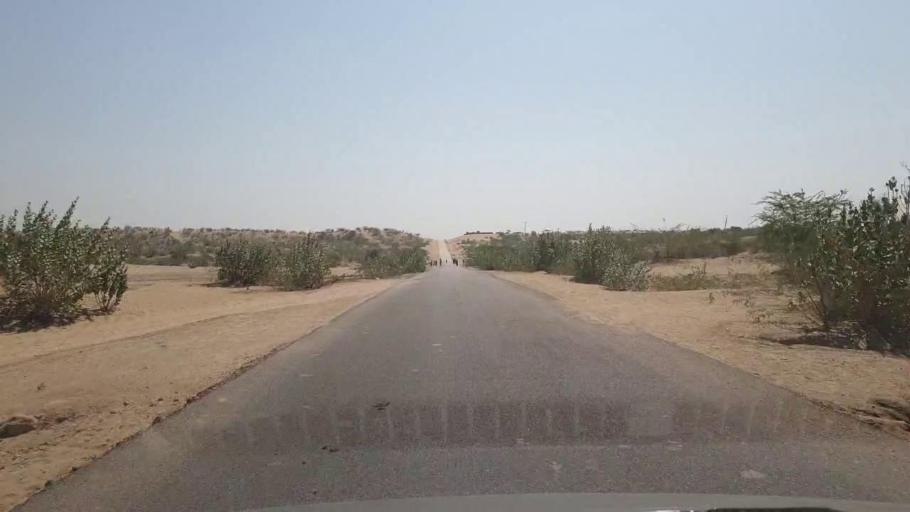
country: PK
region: Sindh
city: Chor
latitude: 25.5788
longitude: 70.1900
